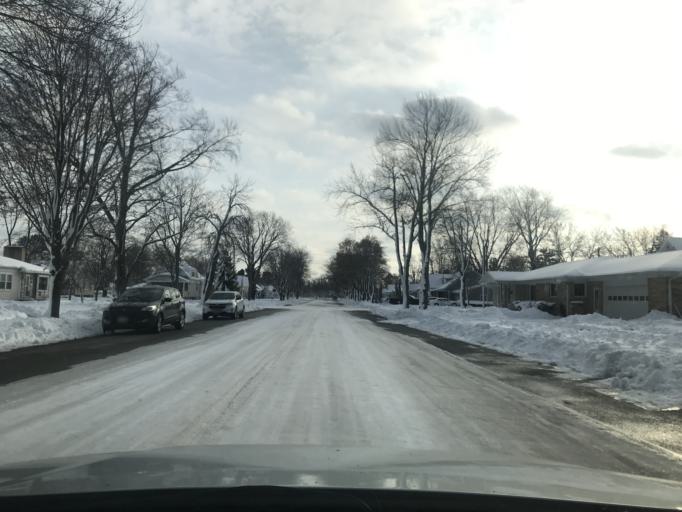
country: US
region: Wisconsin
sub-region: Marinette County
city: Peshtigo
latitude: 45.0534
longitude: -87.7551
